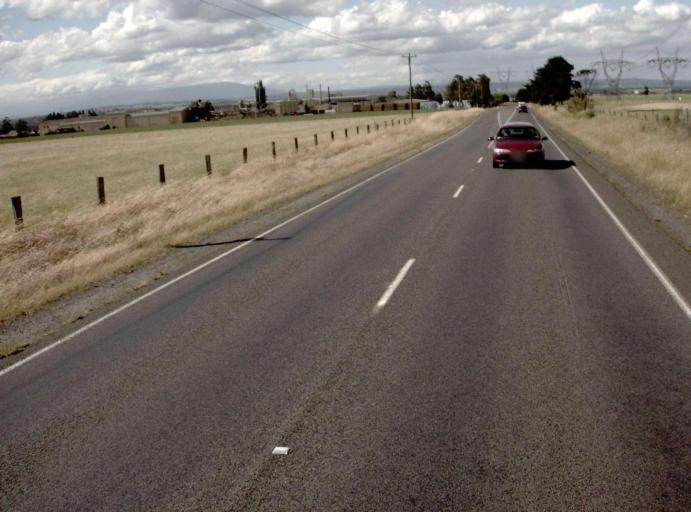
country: AU
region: Victoria
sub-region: Latrobe
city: Morwell
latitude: -38.2699
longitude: 146.4338
